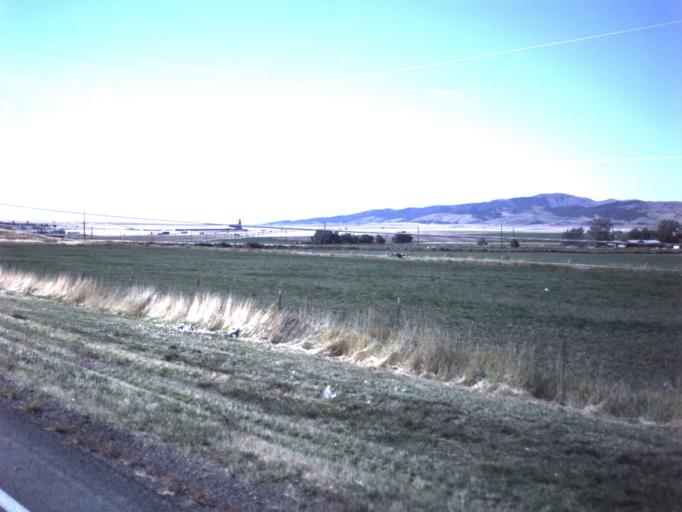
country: US
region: Utah
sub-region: Juab County
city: Nephi
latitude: 39.6922
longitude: -111.8362
